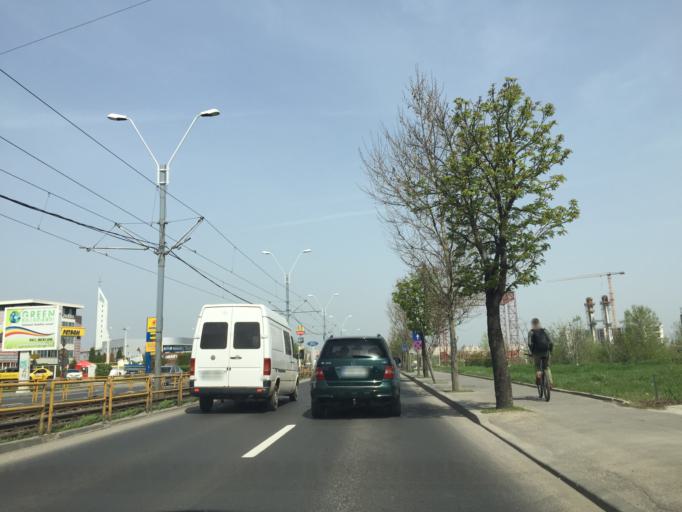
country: RO
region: Ilfov
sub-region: Comuna Chiajna
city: Rosu
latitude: 44.4432
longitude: 26.0361
